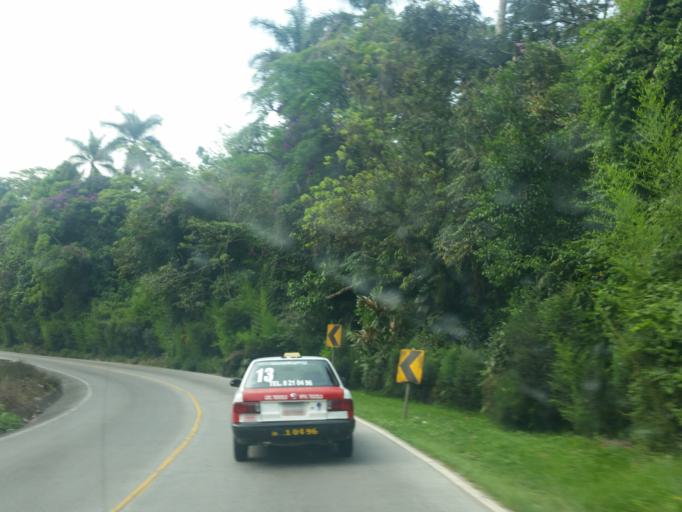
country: MX
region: Veracruz
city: Coatepec
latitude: 19.4395
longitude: -96.9548
